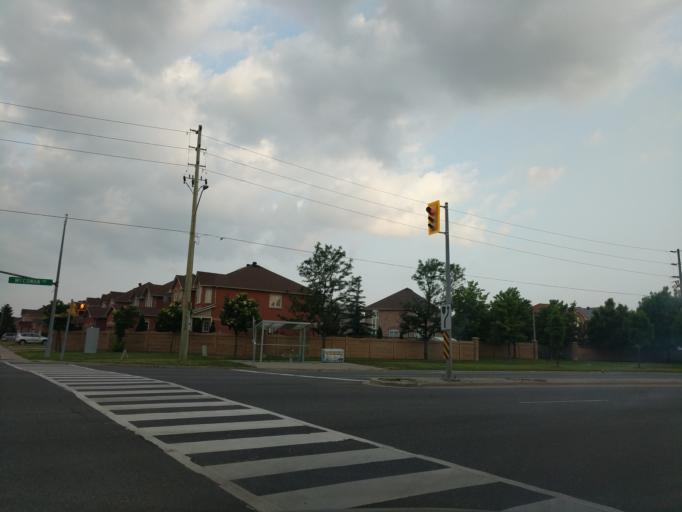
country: CA
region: Ontario
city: Markham
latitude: 43.8461
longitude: -79.2788
